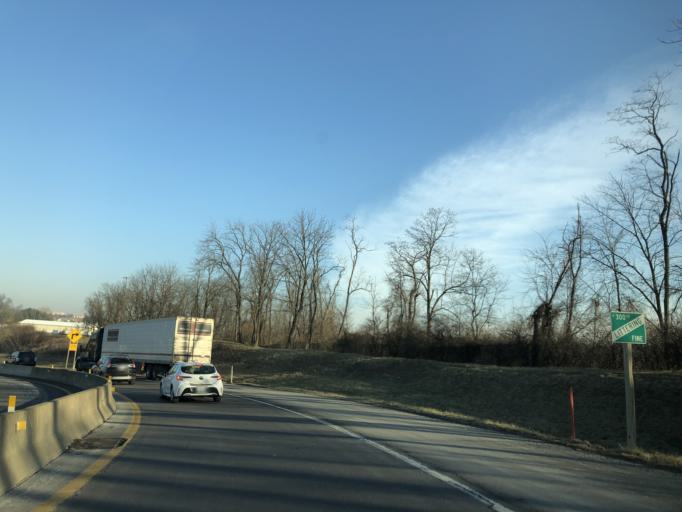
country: US
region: Pennsylvania
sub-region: Chester County
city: Elverson
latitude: 40.1582
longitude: -75.8814
